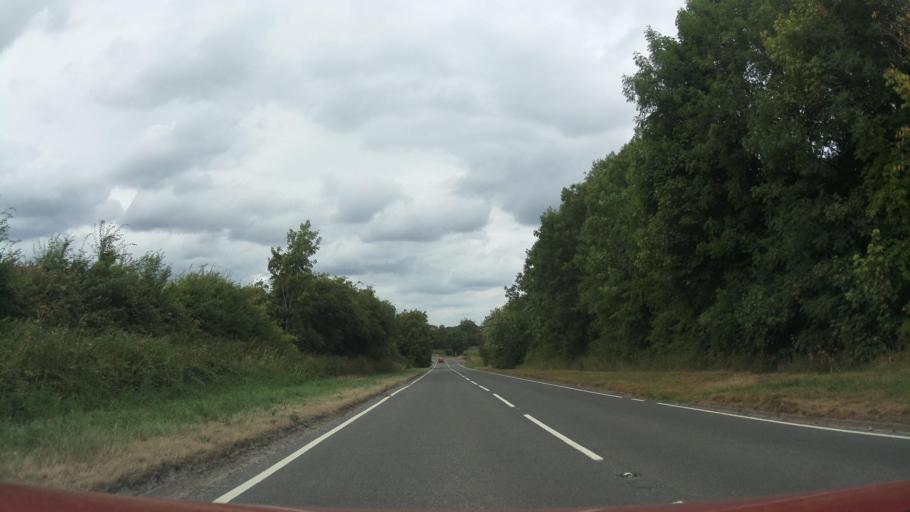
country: GB
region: England
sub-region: Leicestershire
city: Castle Donington
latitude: 52.8044
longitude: -1.3759
